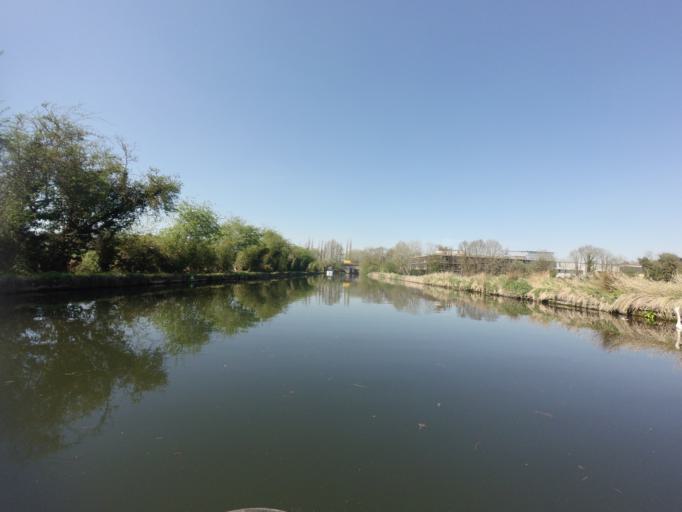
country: GB
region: England
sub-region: Hertfordshire
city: Kings Langley
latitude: 51.7050
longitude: -0.4418
